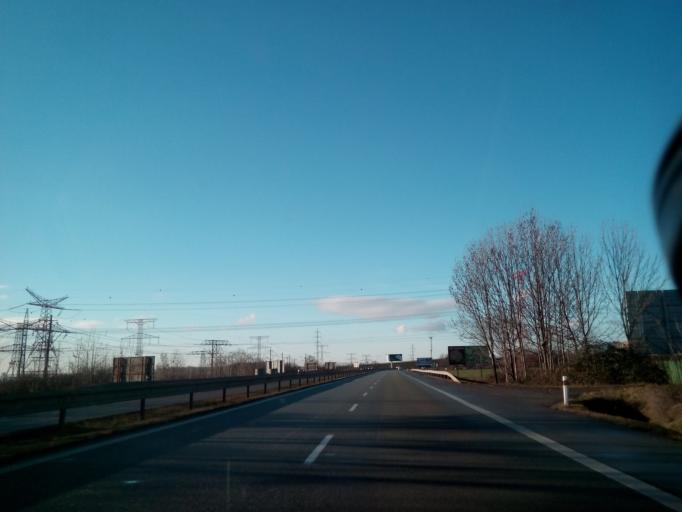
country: SK
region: Kosicky
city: Kosice
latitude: 48.6310
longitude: 21.1907
